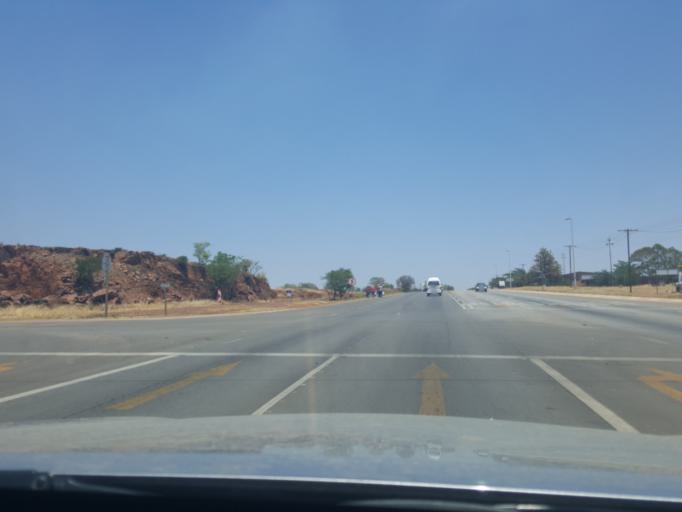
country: ZA
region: North-West
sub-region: Ngaka Modiri Molema District Municipality
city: Zeerust
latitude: -25.5500
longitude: 26.0729
